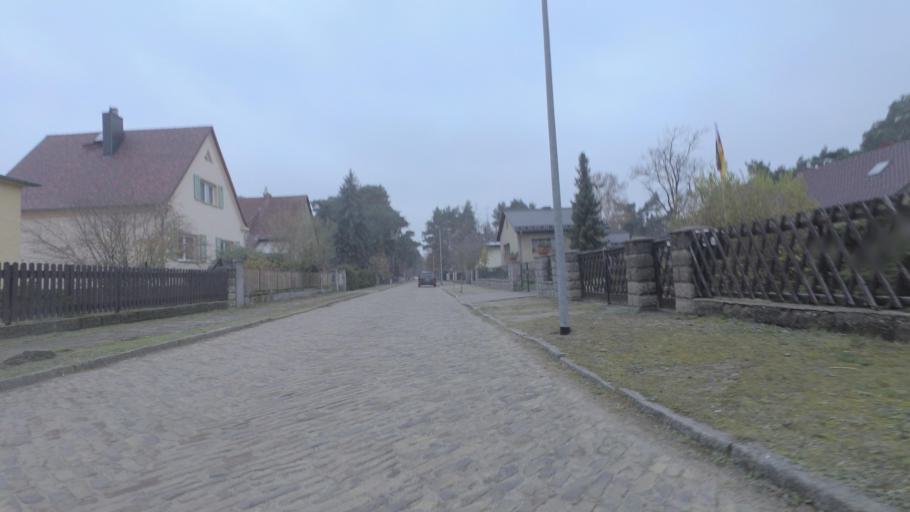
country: DE
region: Brandenburg
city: Am Mellensee
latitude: 52.1673
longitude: 13.3933
